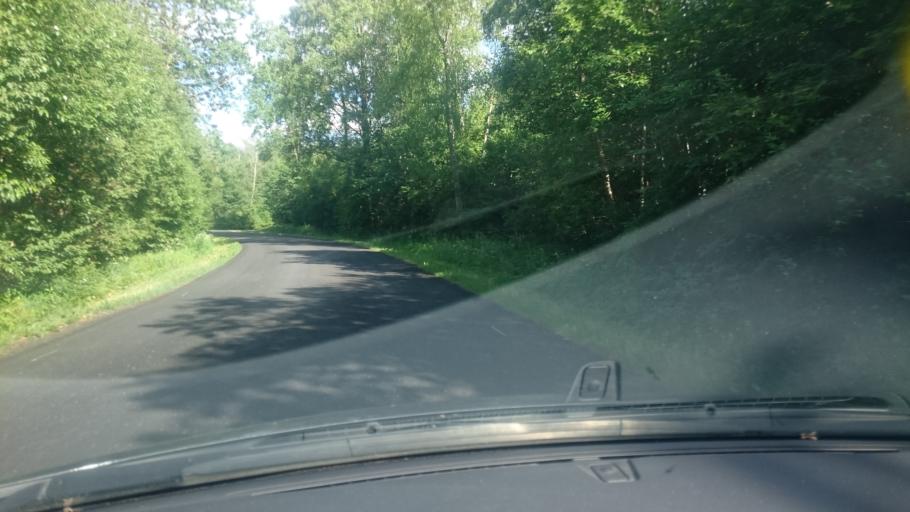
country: EE
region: Harju
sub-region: Rae vald
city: Vaida
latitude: 59.2271
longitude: 24.9986
